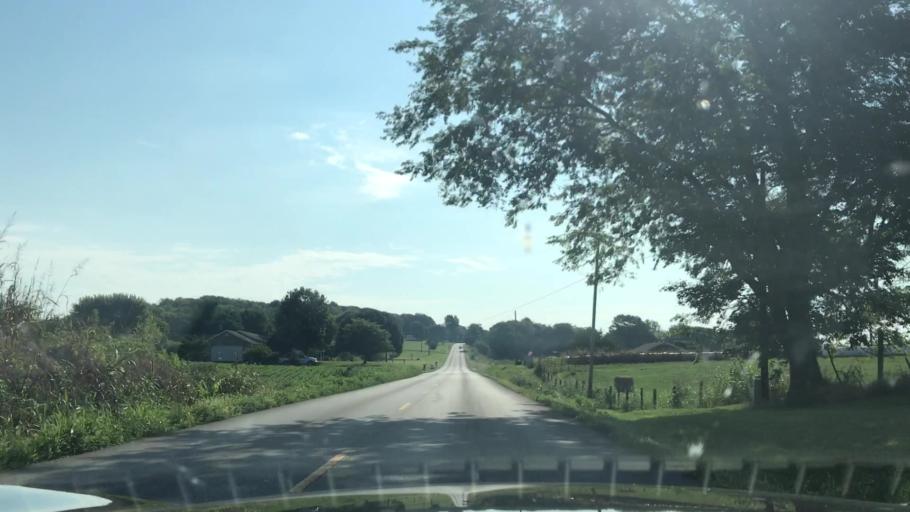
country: US
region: Kentucky
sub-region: Hart County
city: Horse Cave
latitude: 37.1668
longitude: -85.8279
